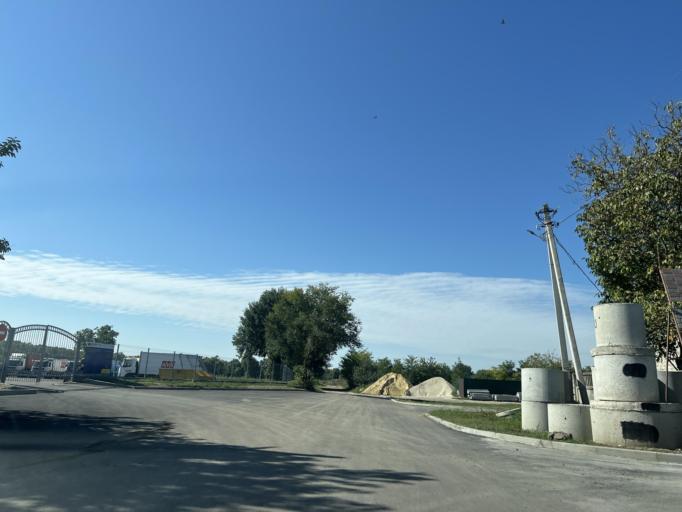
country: RO
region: Iasi
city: Ungheni-Prut
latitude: 47.1934
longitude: 27.7969
